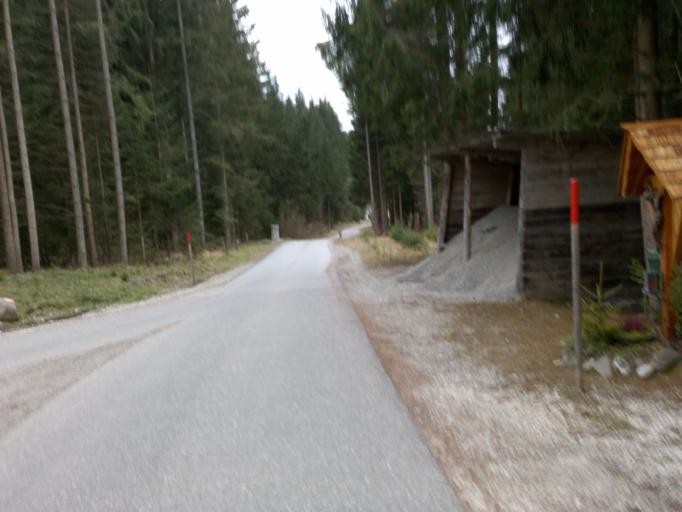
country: AT
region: Carinthia
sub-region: Politischer Bezirk Wolfsberg
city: Reichenfels
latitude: 47.0576
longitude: 14.7413
